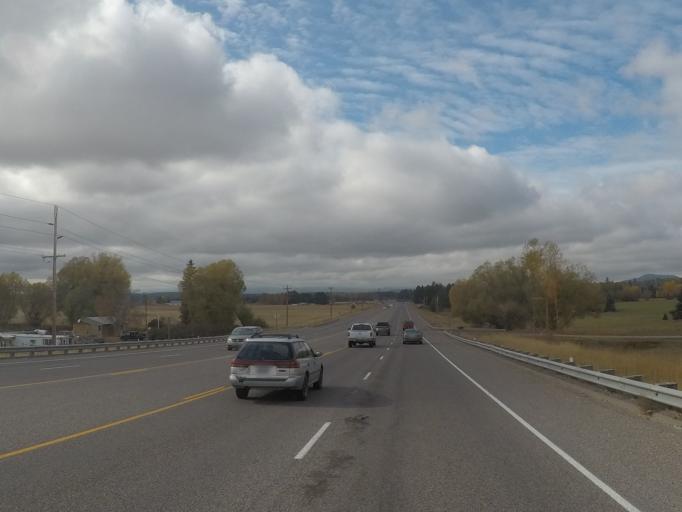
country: US
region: Montana
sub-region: Flathead County
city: Columbia Falls
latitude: 48.3708
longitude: -114.2225
